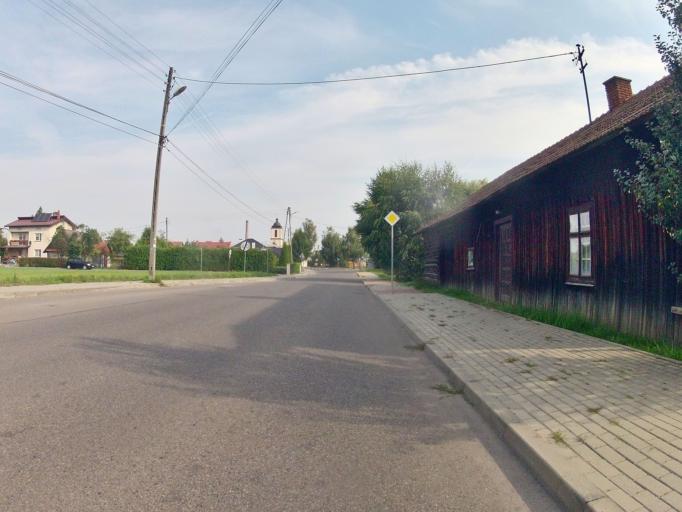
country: PL
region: Subcarpathian Voivodeship
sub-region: Powiat jasielski
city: Jaslo
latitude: 49.7162
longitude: 21.4616
